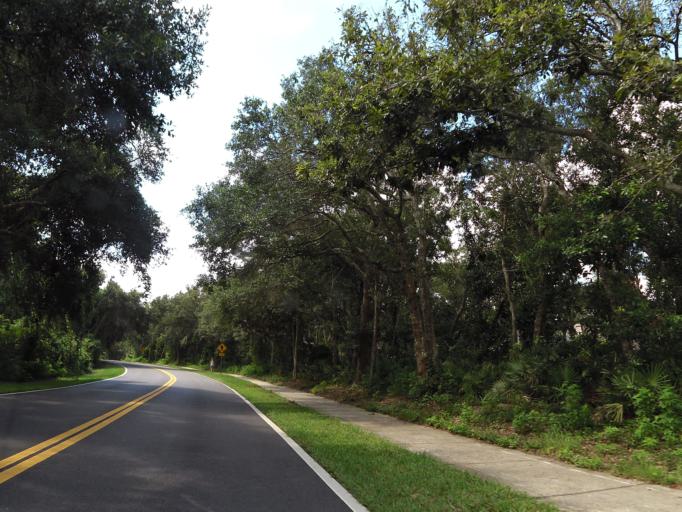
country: US
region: Florida
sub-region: Nassau County
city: Fernandina Beach
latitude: 30.5881
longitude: -81.4463
